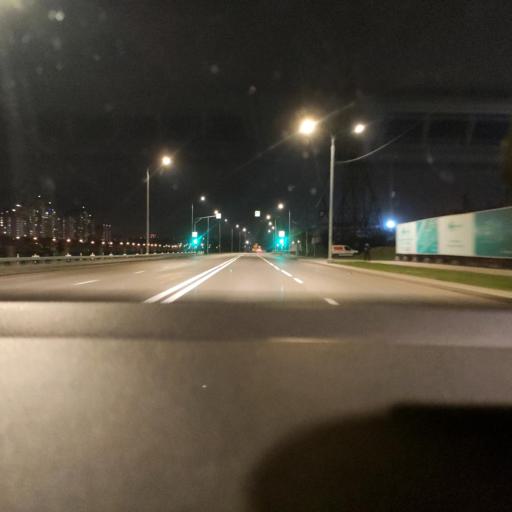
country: RU
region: Moskovskaya
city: Kozhukhovo
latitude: 55.6871
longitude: 37.6587
